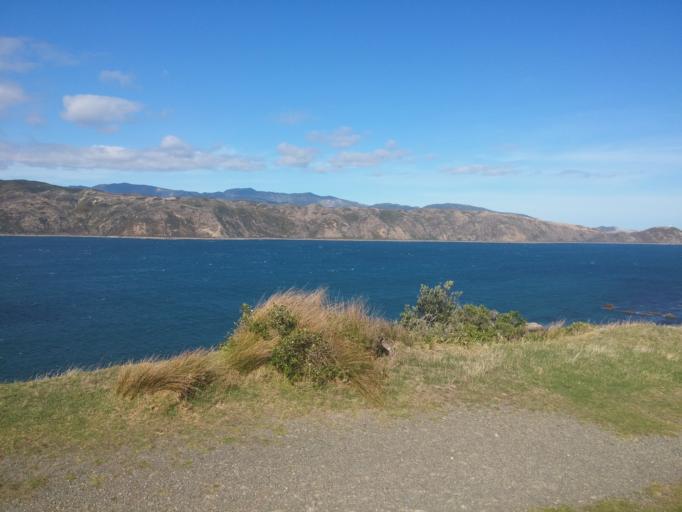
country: NZ
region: Wellington
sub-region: Wellington City
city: Wellington
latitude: -41.3293
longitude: 174.8375
